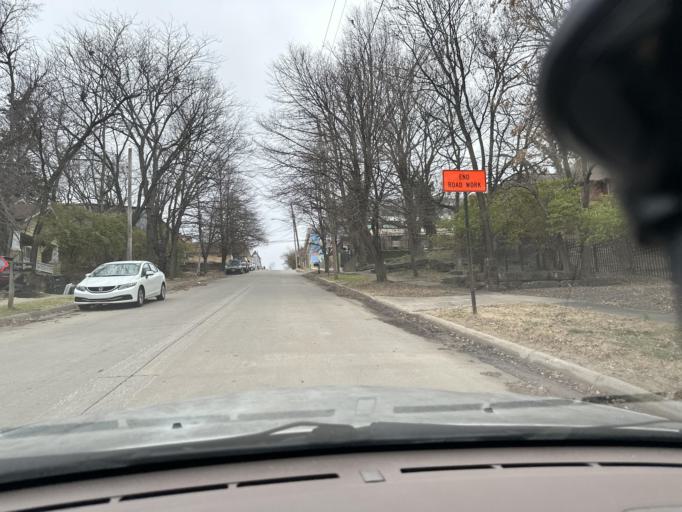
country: US
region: Arkansas
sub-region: Washington County
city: Fayetteville
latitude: 36.0599
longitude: -94.1607
